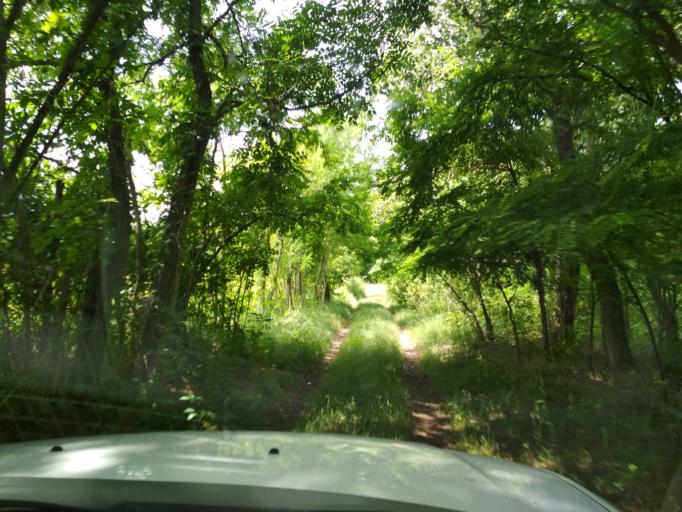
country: HU
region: Pest
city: Tapioszentmarton
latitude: 47.3729
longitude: 19.7725
